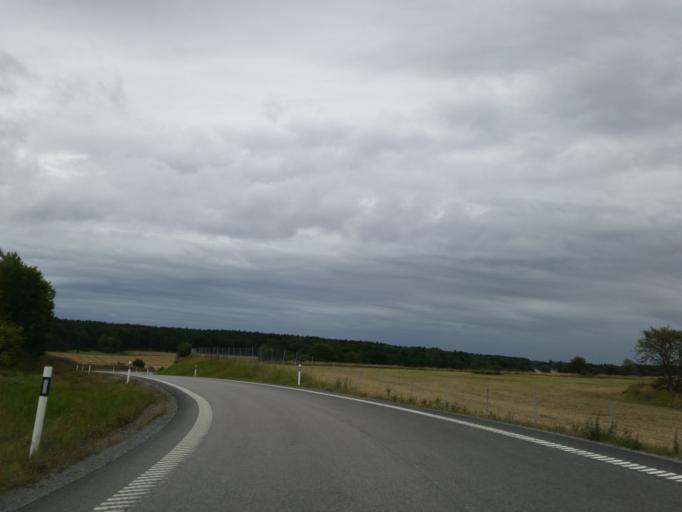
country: SE
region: Uppsala
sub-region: Enkopings Kommun
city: Grillby
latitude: 59.6349
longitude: 17.2722
